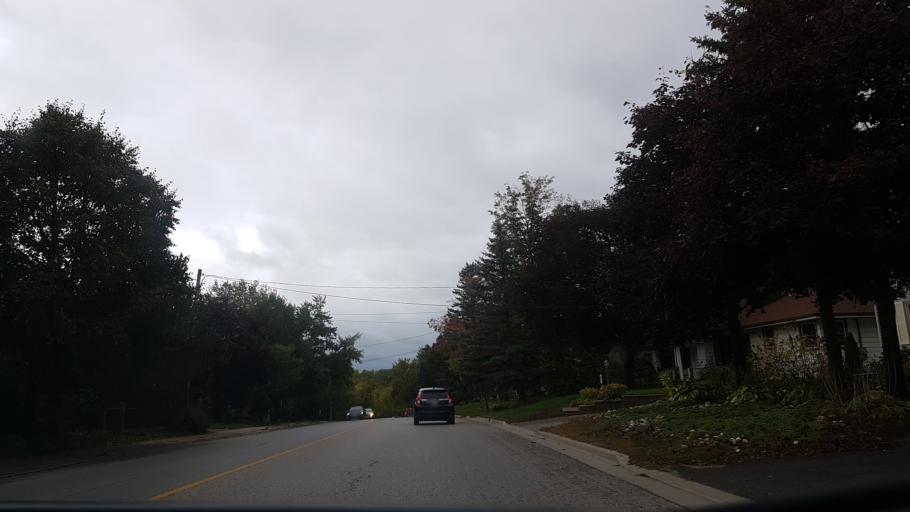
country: CA
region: Ontario
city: Uxbridge
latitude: 44.1054
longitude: -79.1162
